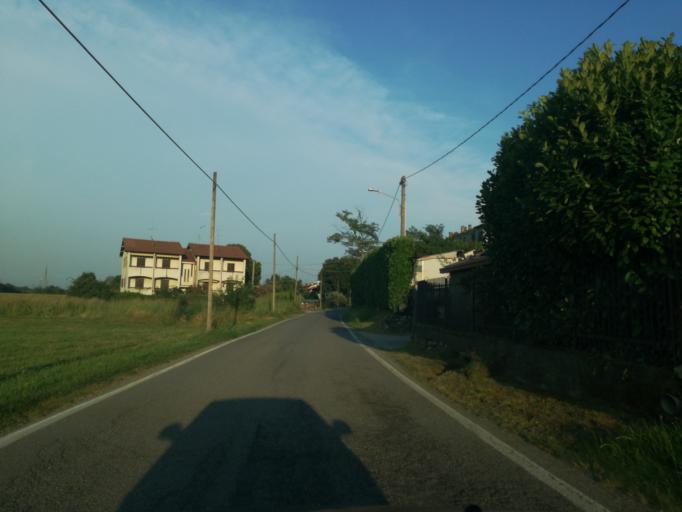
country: IT
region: Lombardy
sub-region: Provincia di Lecco
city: Paderno d'Adda
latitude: 45.6749
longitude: 9.4546
